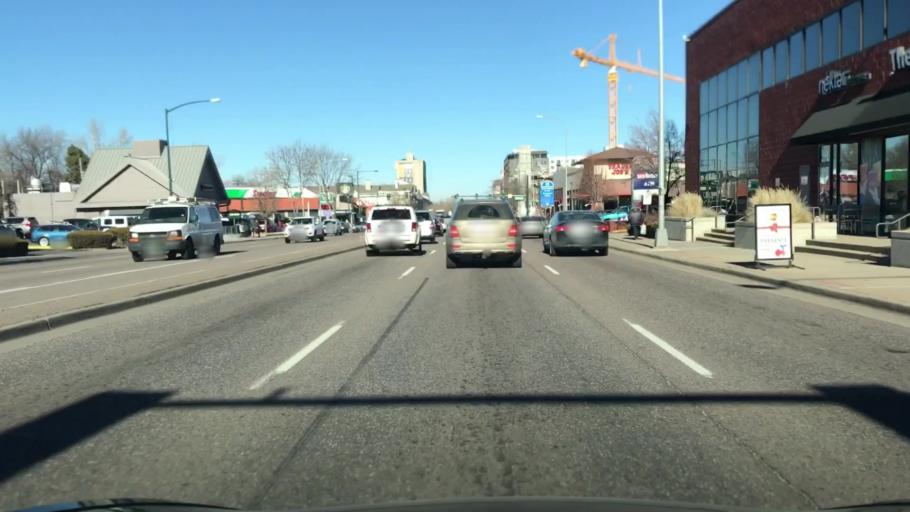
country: US
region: Colorado
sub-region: Arapahoe County
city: Glendale
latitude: 39.7276
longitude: -104.9407
